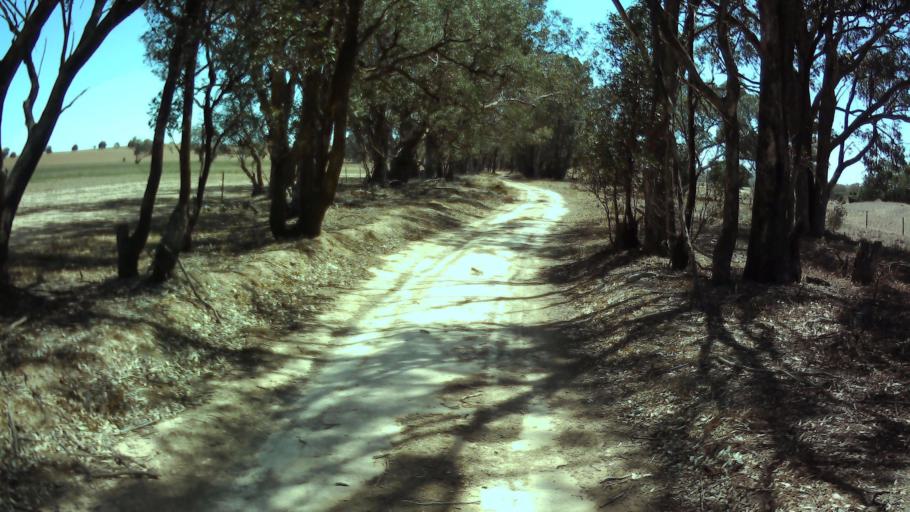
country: AU
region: New South Wales
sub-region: Weddin
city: Grenfell
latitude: -33.9917
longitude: 148.1637
